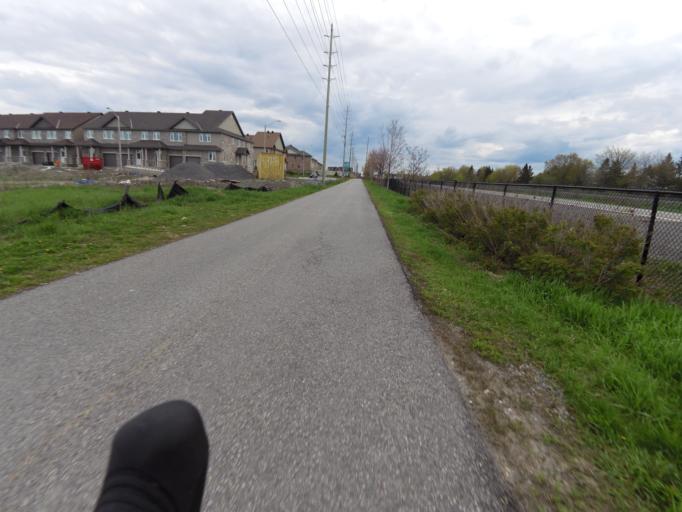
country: CA
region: Ontario
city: Bells Corners
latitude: 45.2881
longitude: -75.7445
